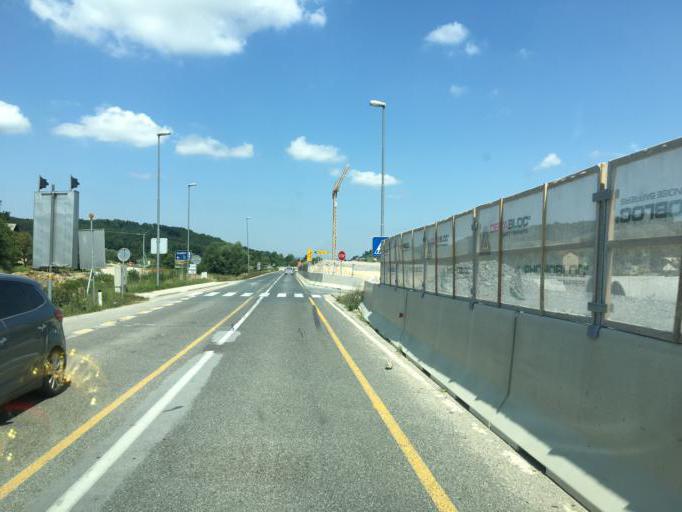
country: SI
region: Podlehnik
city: Podlehnik
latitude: 46.3311
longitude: 15.8778
